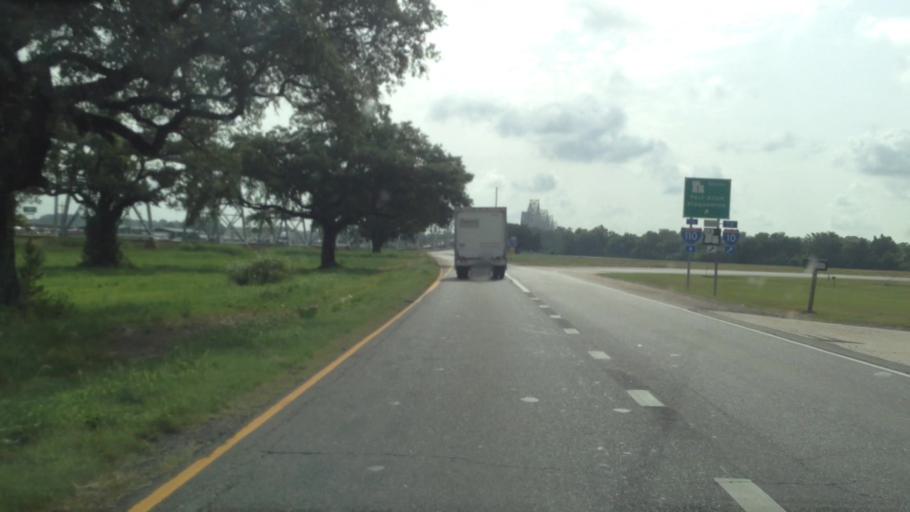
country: US
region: Louisiana
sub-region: West Baton Rouge Parish
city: Port Allen
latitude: 30.5054
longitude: -91.2139
